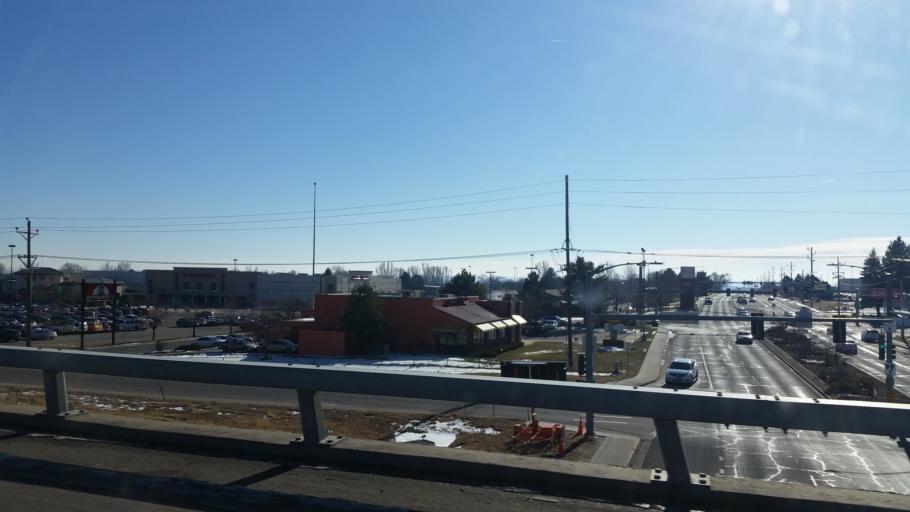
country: US
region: Colorado
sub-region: Weld County
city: Evans
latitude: 40.3920
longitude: -104.7158
